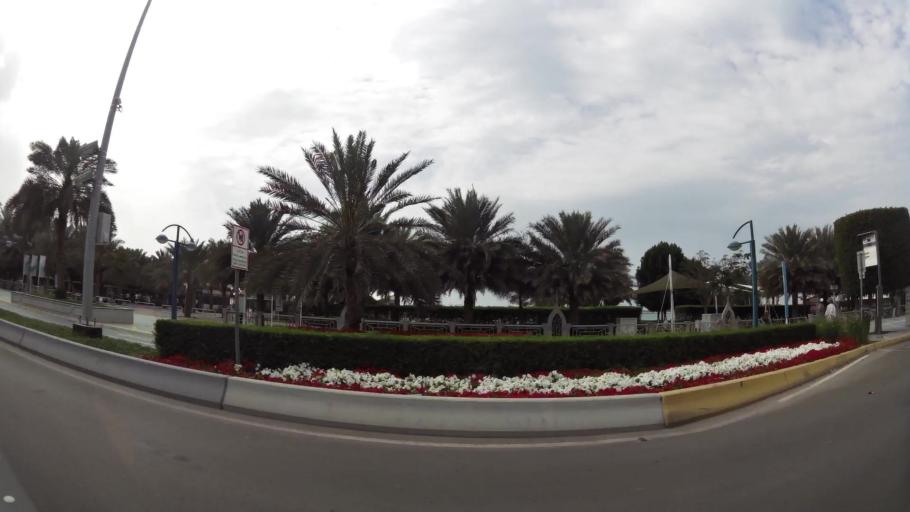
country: AE
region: Abu Dhabi
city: Abu Dhabi
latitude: 24.4762
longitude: 54.3442
